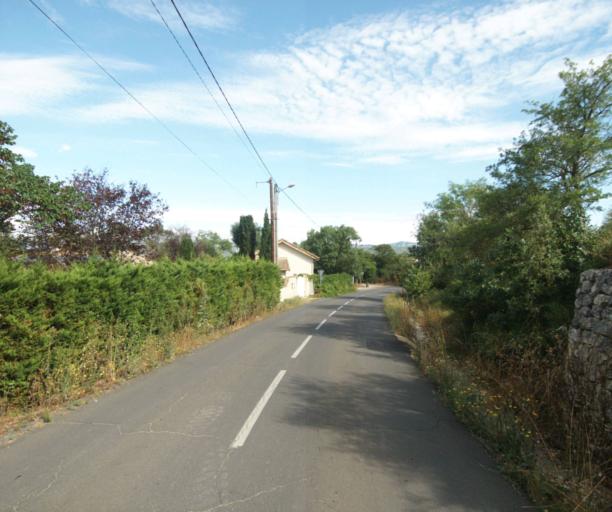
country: FR
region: Languedoc-Roussillon
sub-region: Departement de l'Herault
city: Aniane
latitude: 43.6811
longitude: 3.5938
